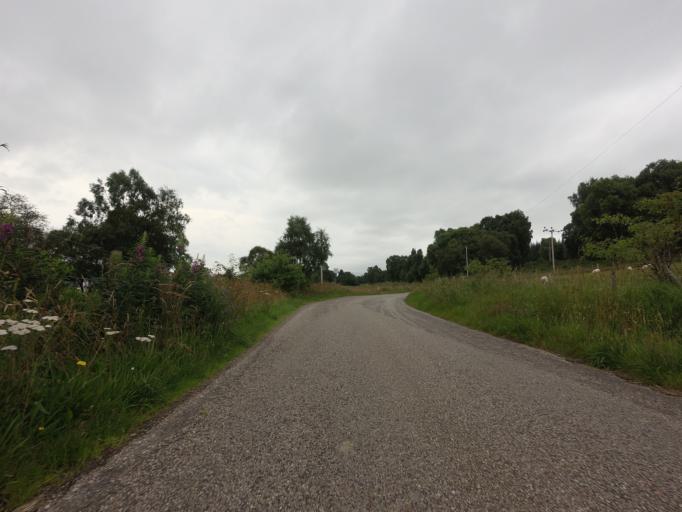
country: GB
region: Scotland
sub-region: Highland
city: Evanton
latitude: 57.9067
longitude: -4.3929
